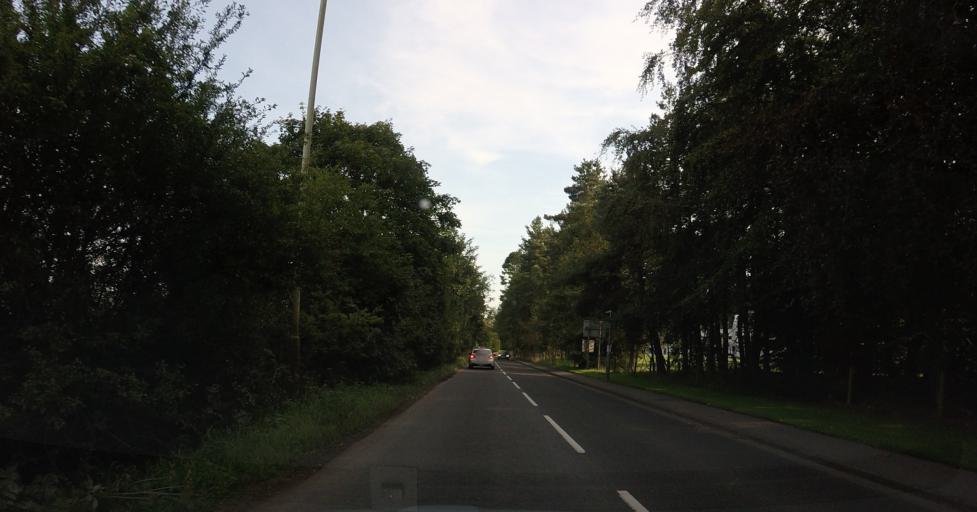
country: GB
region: Scotland
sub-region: Perth and Kinross
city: Auchterarder
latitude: 56.2853
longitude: -3.7453
